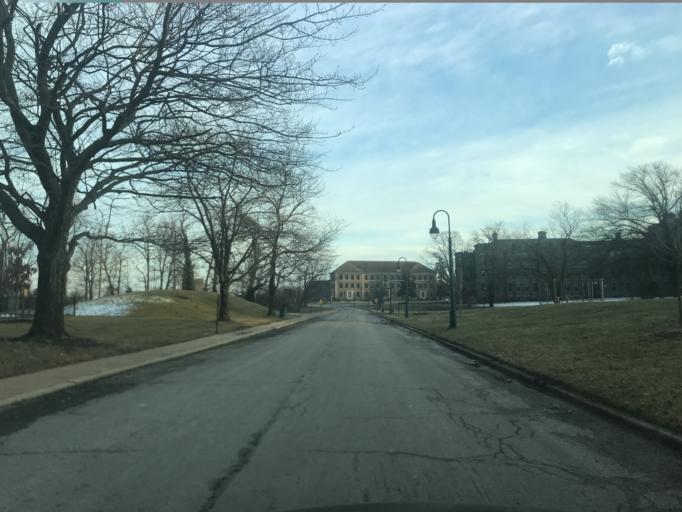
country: US
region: Maryland
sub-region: Baltimore County
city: Catonsville
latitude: 39.2666
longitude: -76.7224
